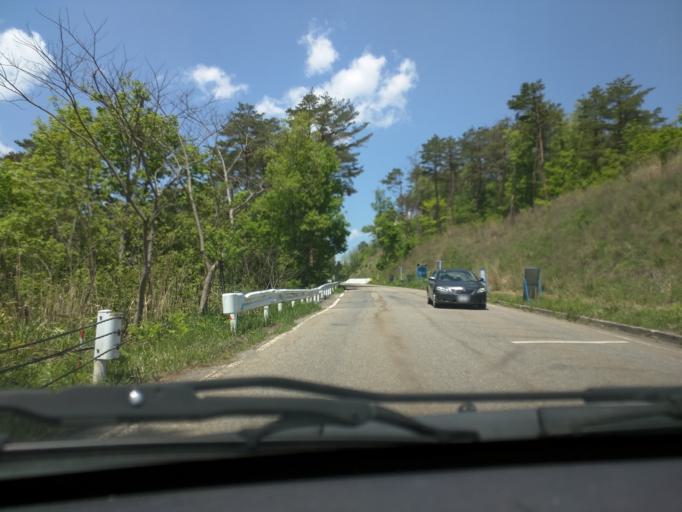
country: JP
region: Fukushima
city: Kitakata
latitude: 37.6329
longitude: 139.8273
